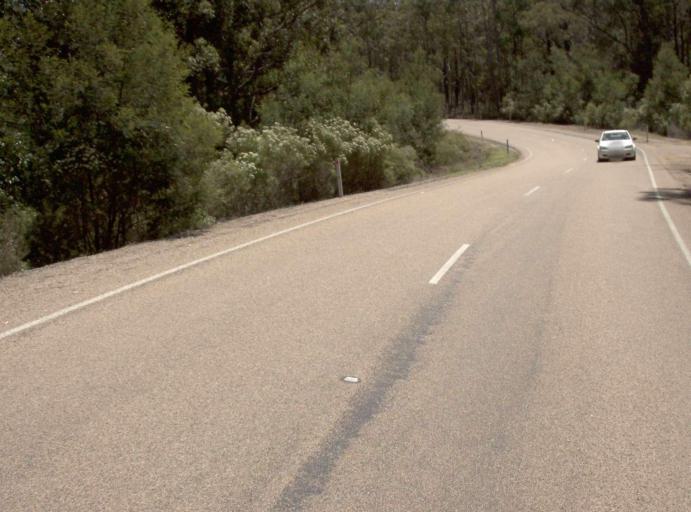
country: AU
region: Victoria
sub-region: East Gippsland
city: Lakes Entrance
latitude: -37.6284
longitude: 147.8873
